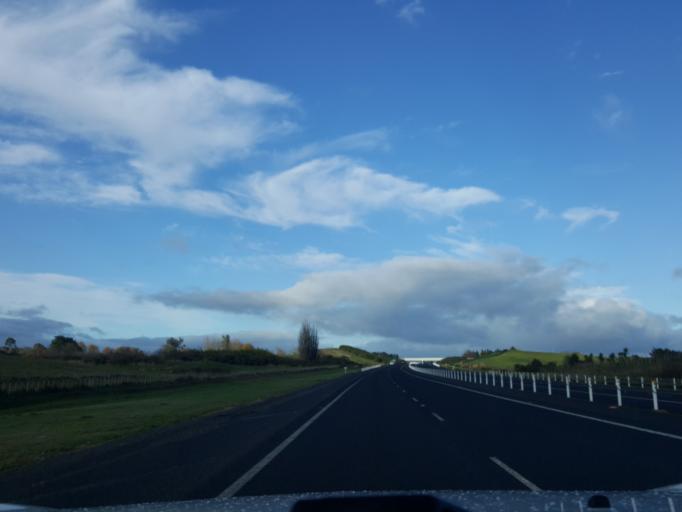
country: NZ
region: Waikato
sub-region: Waikato District
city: Ngaruawahia
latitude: -37.6905
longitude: 175.2145
